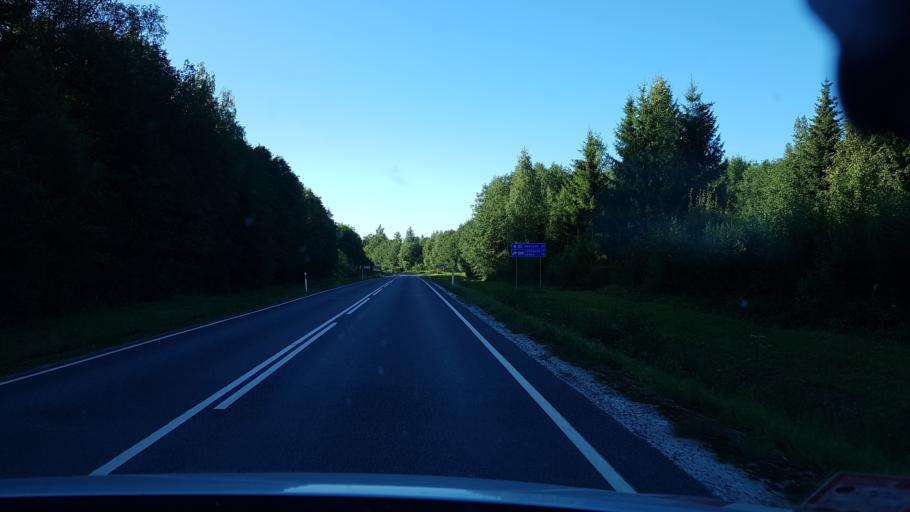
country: EE
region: Ida-Virumaa
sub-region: Kivioli linn
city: Kivioli
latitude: 59.1608
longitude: 26.8880
